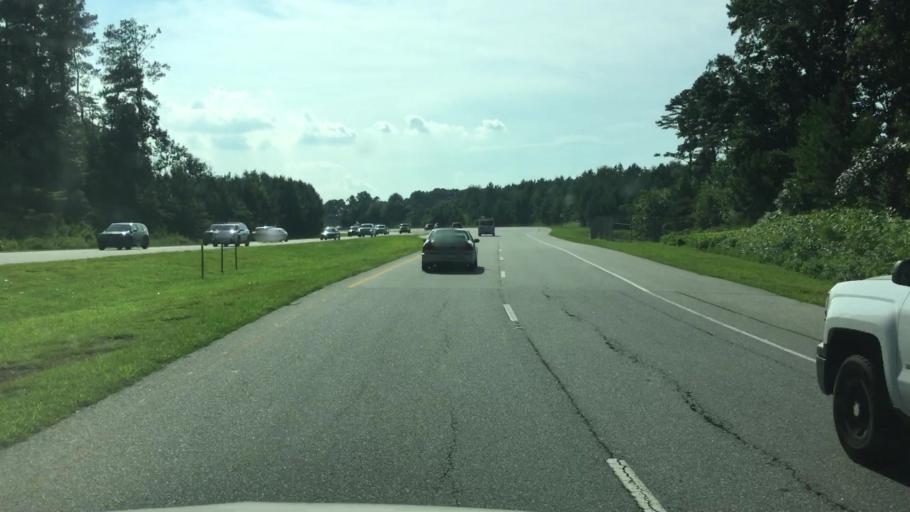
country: US
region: Georgia
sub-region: Gwinnett County
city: Grayson
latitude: 33.9193
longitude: -83.9680
